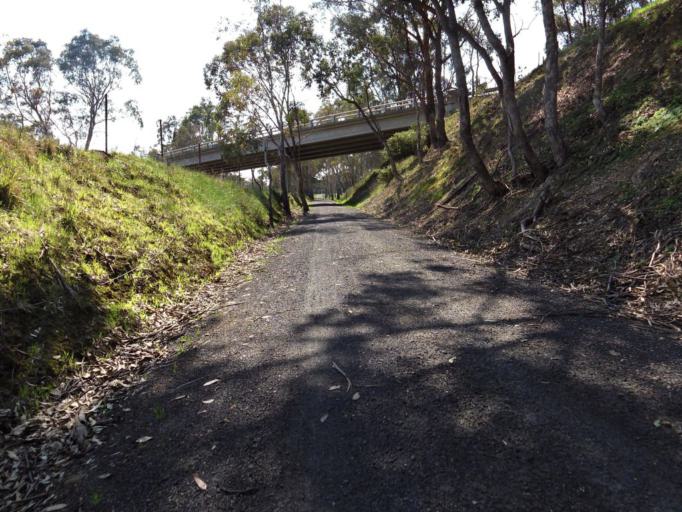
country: AU
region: Victoria
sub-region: Murrindindi
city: Alexandra
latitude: -37.1166
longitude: 145.6056
